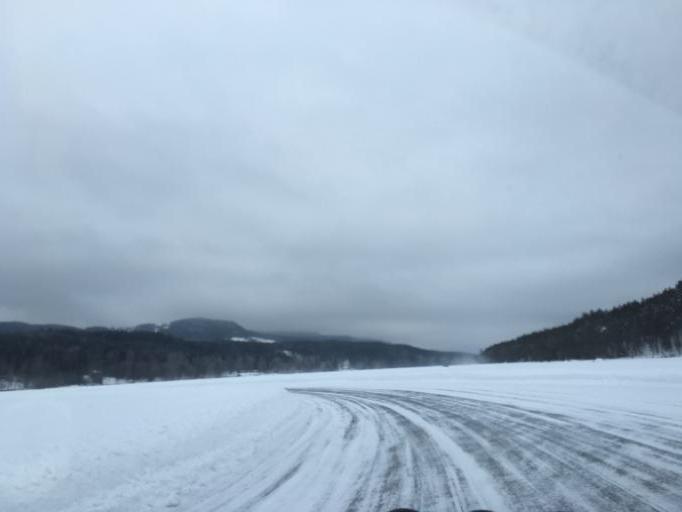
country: SE
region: Dalarna
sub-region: Alvdalens Kommun
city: AElvdalen
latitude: 61.2571
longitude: 14.0935
